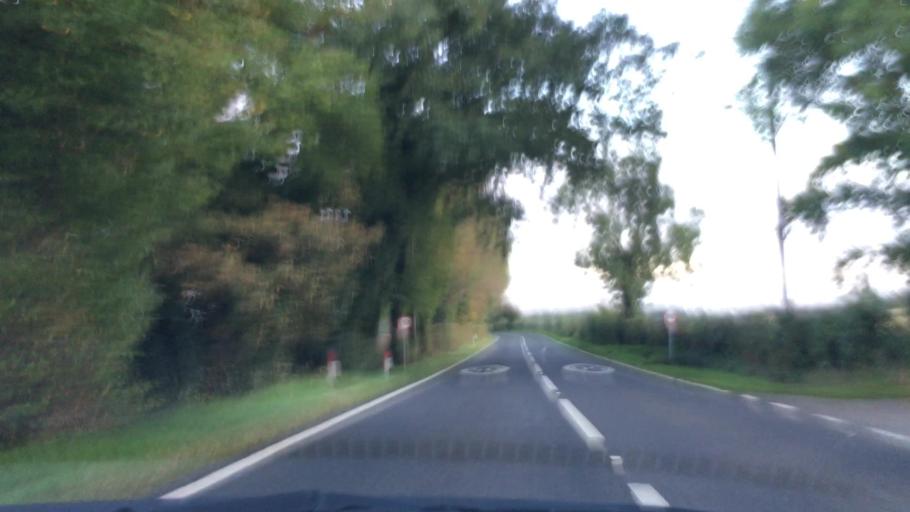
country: GB
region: England
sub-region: North East Lincolnshire
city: Wold Newton
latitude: 53.4612
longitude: -0.0948
